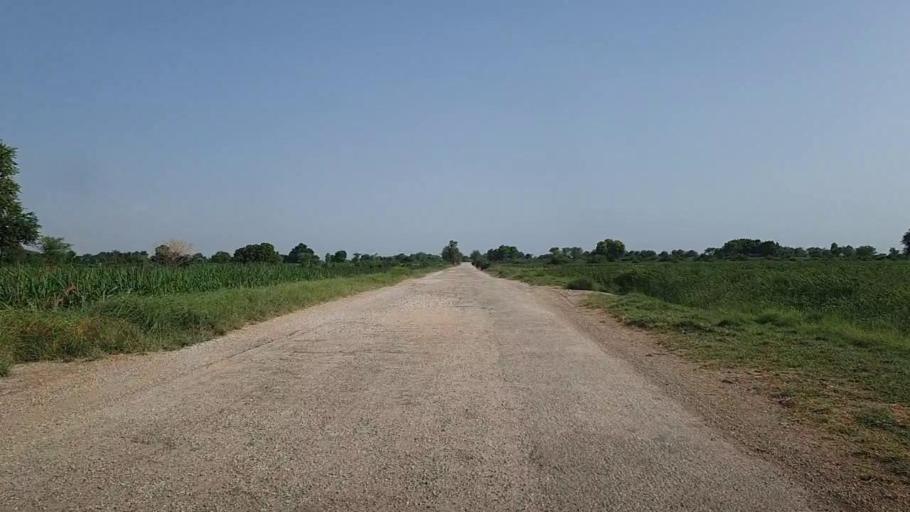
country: PK
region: Sindh
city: Karaundi
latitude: 26.8739
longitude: 68.3283
